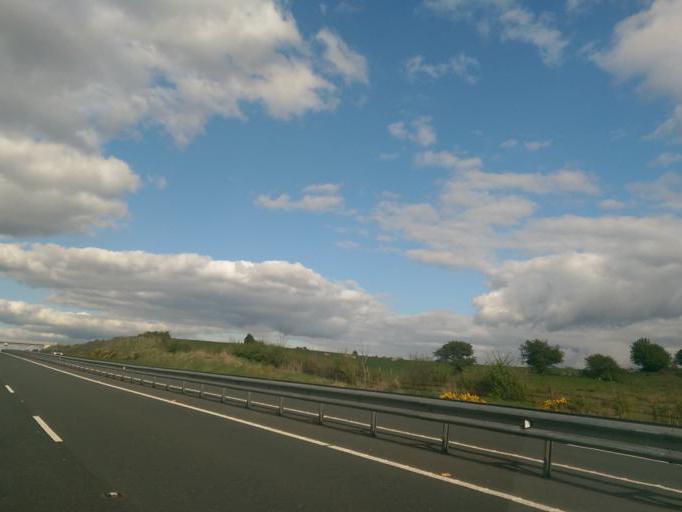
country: IE
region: Connaught
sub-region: County Galway
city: Ballinasloe
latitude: 53.3213
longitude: -8.1498
